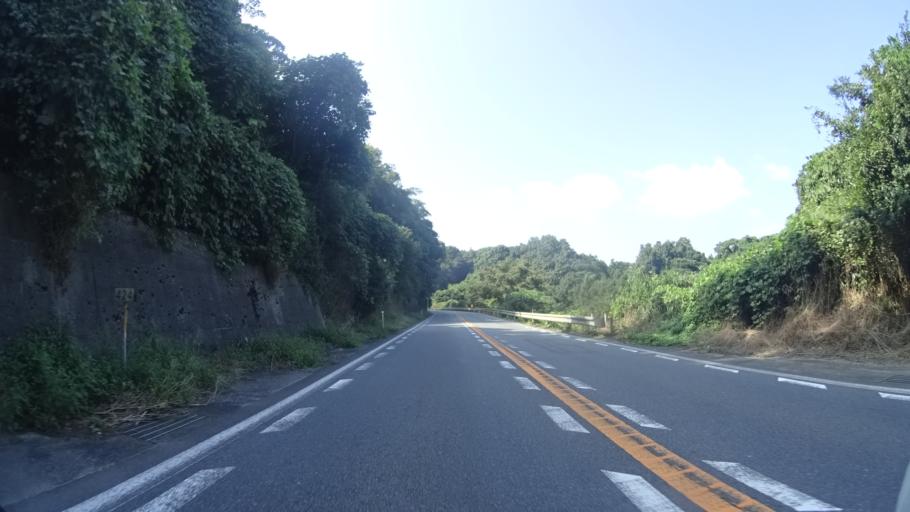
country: JP
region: Shimane
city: Gotsucho
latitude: 35.0683
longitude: 132.3220
